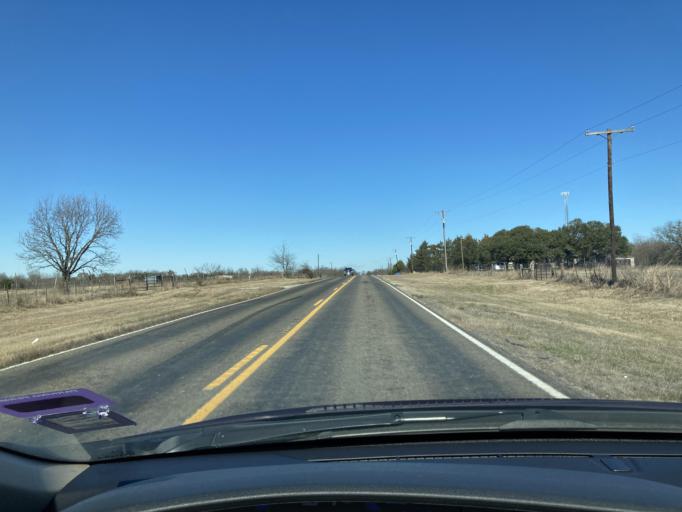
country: US
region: Texas
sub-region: Navarro County
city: Corsicana
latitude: 32.0525
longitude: -96.4976
